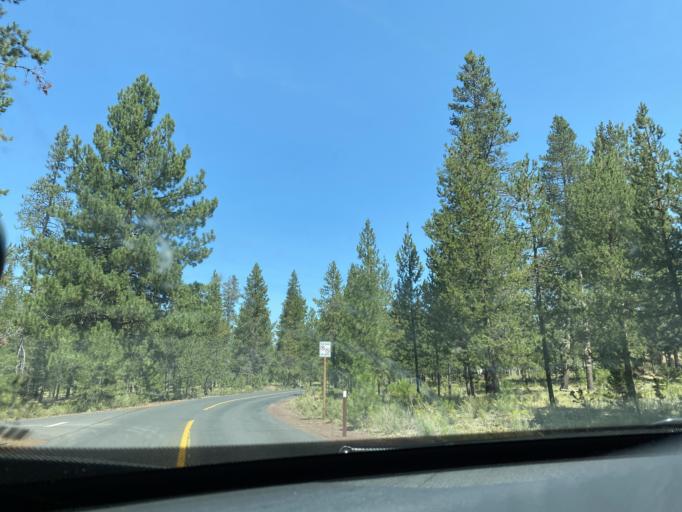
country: US
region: Oregon
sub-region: Deschutes County
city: Sunriver
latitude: 43.8911
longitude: -121.4388
